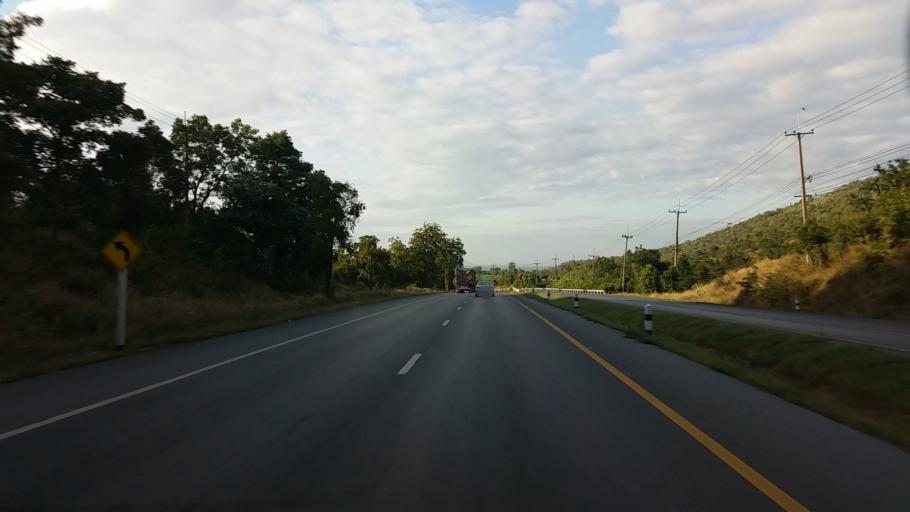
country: TH
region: Lop Buri
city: Phatthana Nikhom
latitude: 14.9687
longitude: 100.9001
